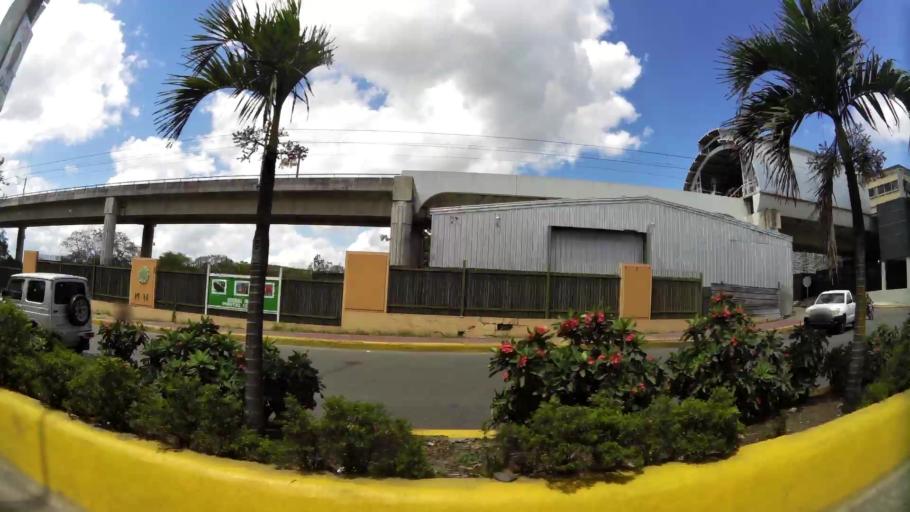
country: DO
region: Nacional
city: Ensanche Luperon
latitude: 18.5175
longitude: -69.9148
